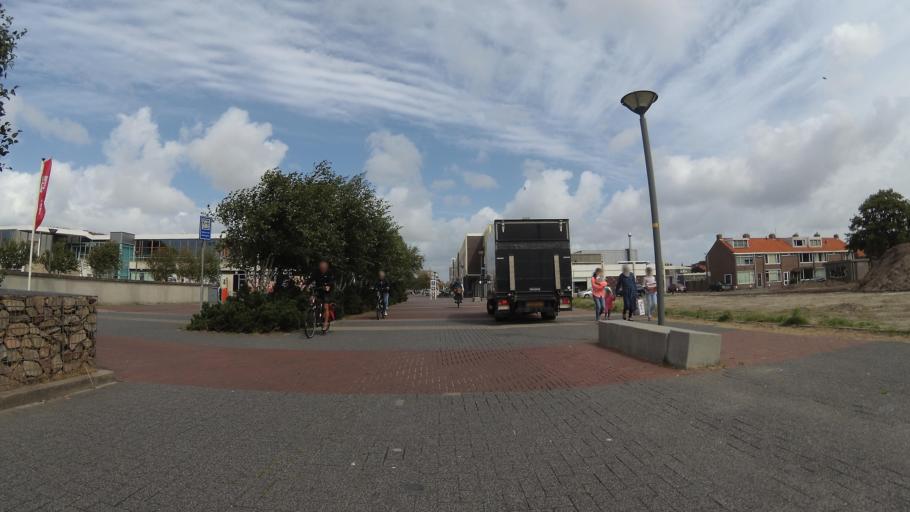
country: NL
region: North Holland
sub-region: Gemeente Den Helder
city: Den Helder
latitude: 52.9428
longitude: 4.7416
